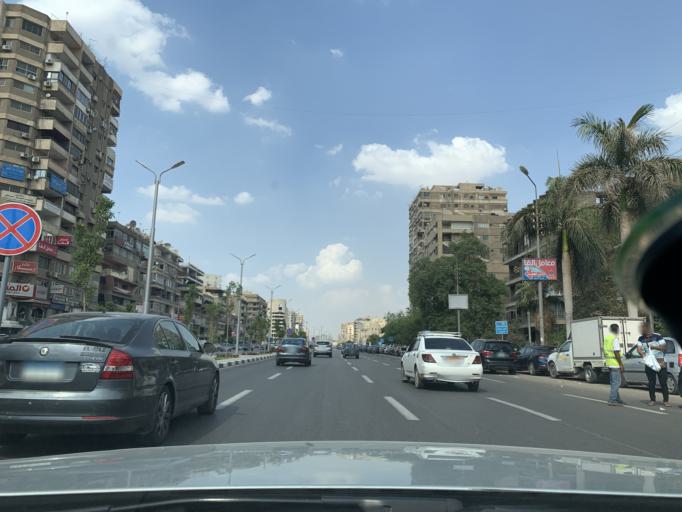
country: EG
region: Muhafazat al Qahirah
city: Cairo
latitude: 30.1063
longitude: 31.3344
